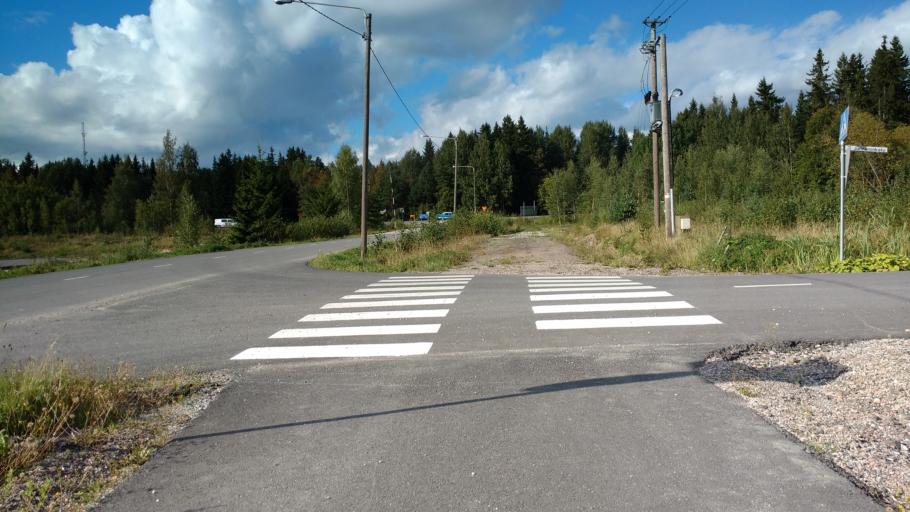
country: FI
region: Varsinais-Suomi
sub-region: Salo
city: Salo
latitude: 60.3809
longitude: 23.1914
